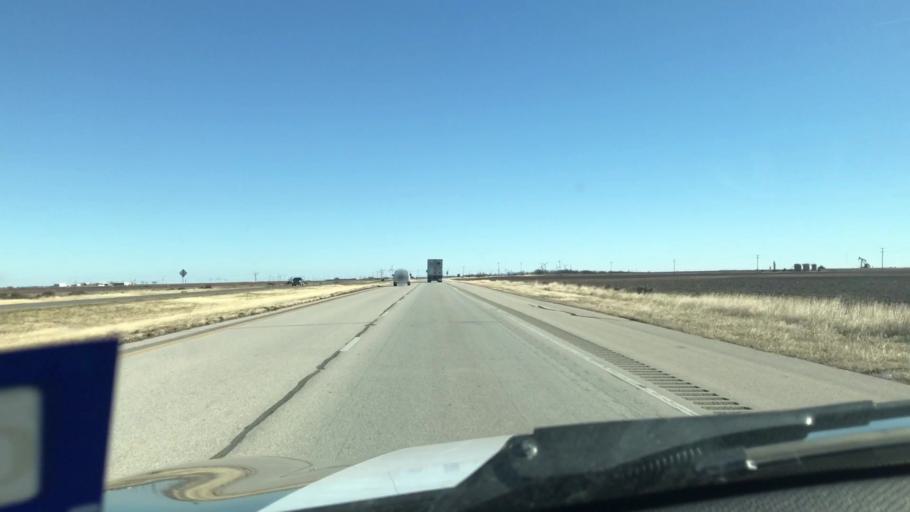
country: US
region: Texas
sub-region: Scurry County
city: Snyder
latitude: 32.6583
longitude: -100.7844
